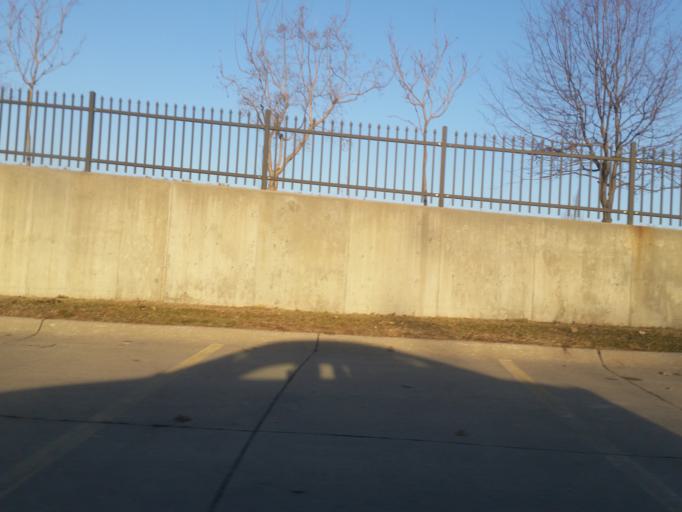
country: US
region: Nebraska
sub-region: Douglas County
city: Omaha
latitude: 41.2250
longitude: -95.9328
